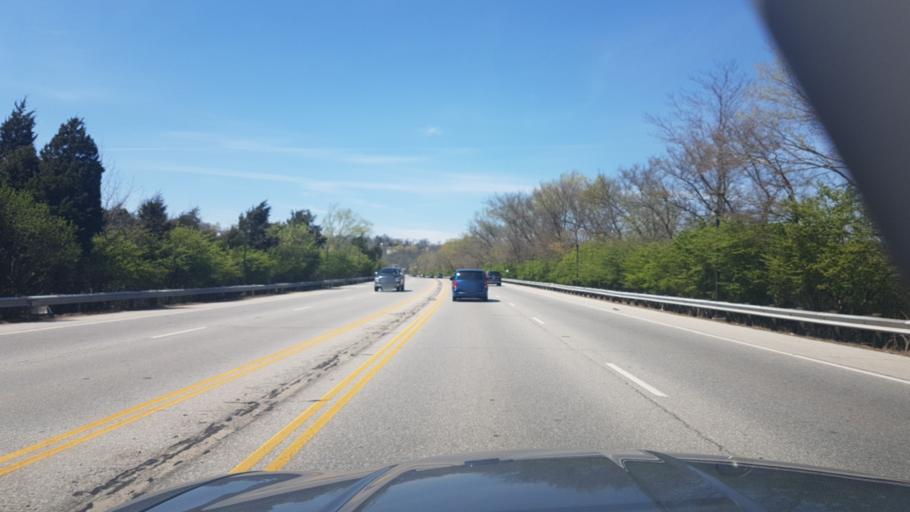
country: US
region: Ohio
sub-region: Hamilton County
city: Turpin Hills
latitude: 39.1146
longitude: -84.4065
